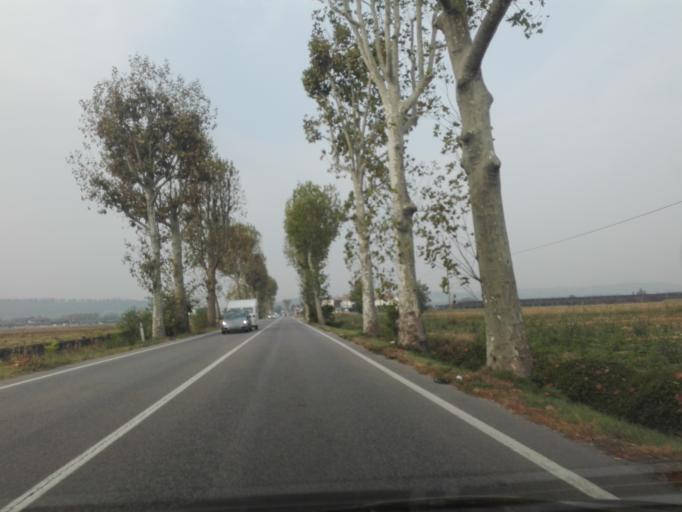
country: IT
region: Veneto
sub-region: Provincia di Verona
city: Sona
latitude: 45.4461
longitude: 10.8585
